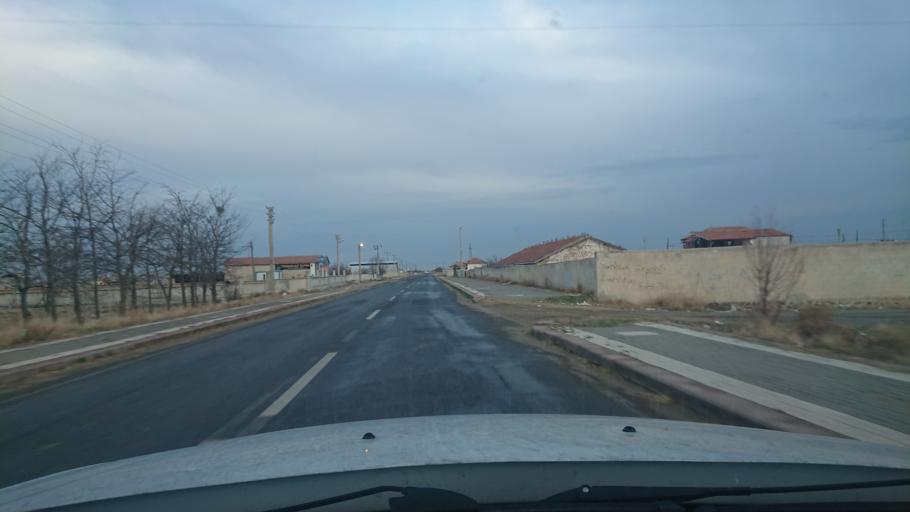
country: TR
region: Aksaray
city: Yesilova
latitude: 38.2935
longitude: 33.7596
